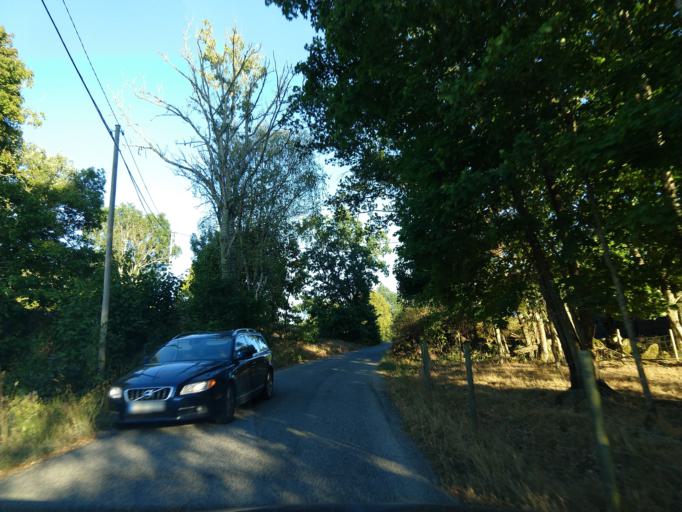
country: SE
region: Blekinge
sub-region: Ronneby Kommun
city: Brakne-Hoby
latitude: 56.2604
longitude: 15.1294
